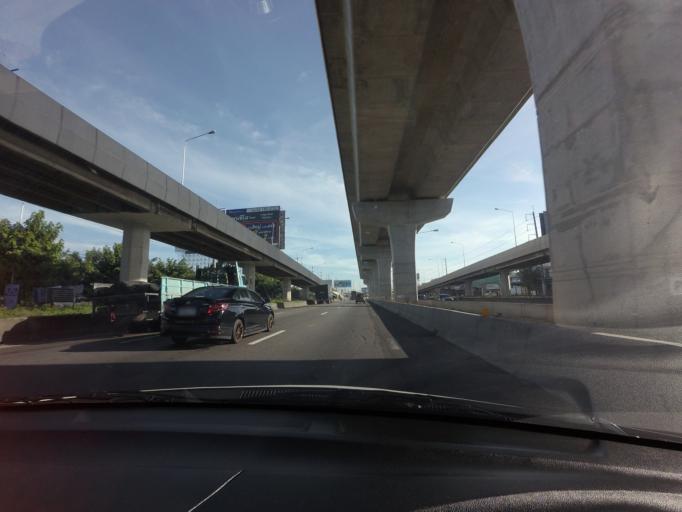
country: TH
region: Nonthaburi
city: Bang Bua Thong
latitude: 13.9016
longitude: 100.4073
